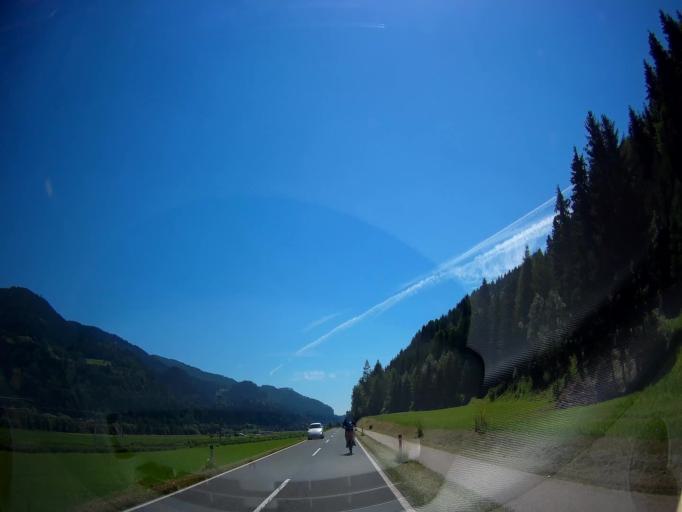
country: AT
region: Carinthia
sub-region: Politischer Bezirk Sankt Veit an der Glan
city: Micheldorf
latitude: 46.9329
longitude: 14.4242
